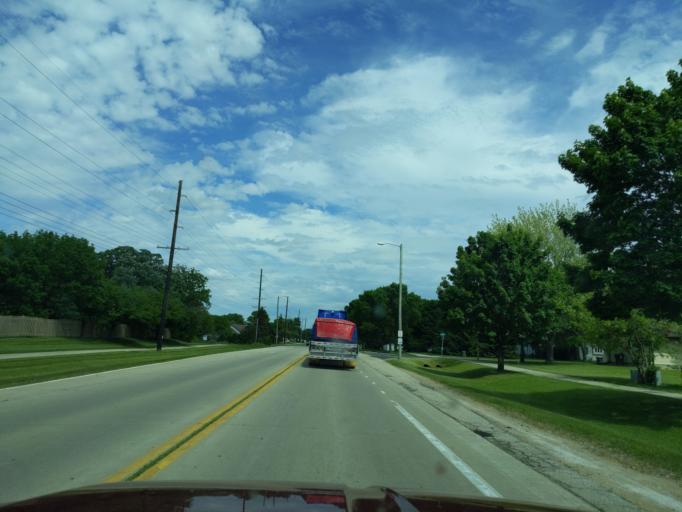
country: US
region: Wisconsin
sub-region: Dane County
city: Sun Prairie
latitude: 43.1872
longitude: -89.2509
